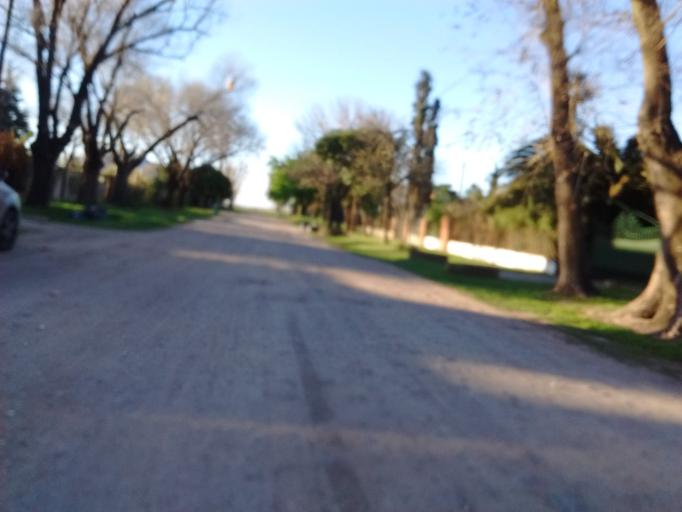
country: AR
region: Santa Fe
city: Funes
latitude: -32.9233
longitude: -60.7863
